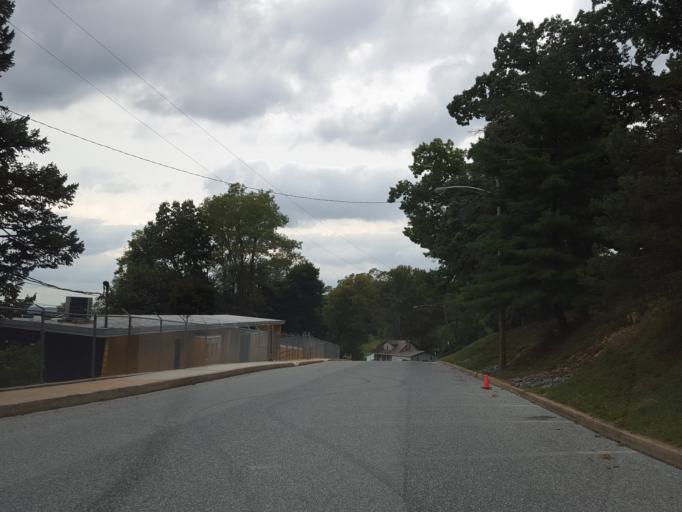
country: US
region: Pennsylvania
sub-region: York County
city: Red Lion
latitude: 39.8968
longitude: -76.6056
